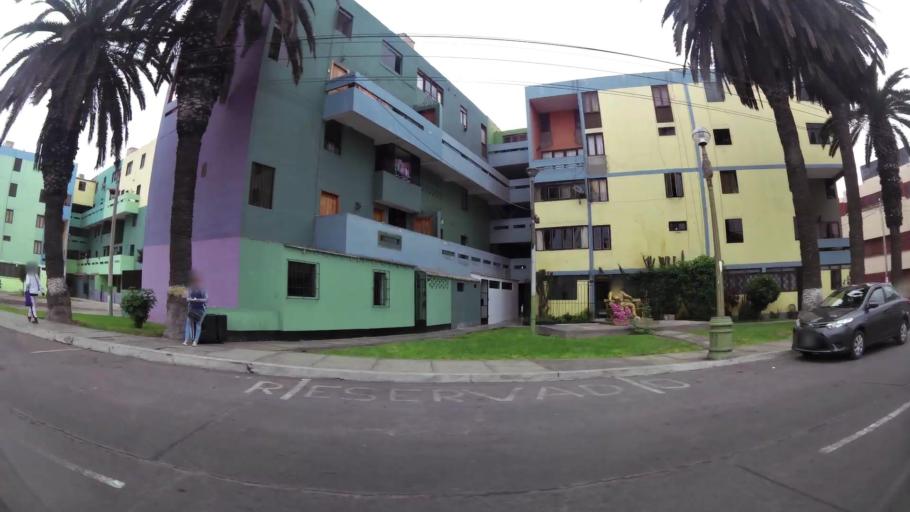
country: PE
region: Callao
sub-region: Callao
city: Callao
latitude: -12.0659
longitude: -77.1557
